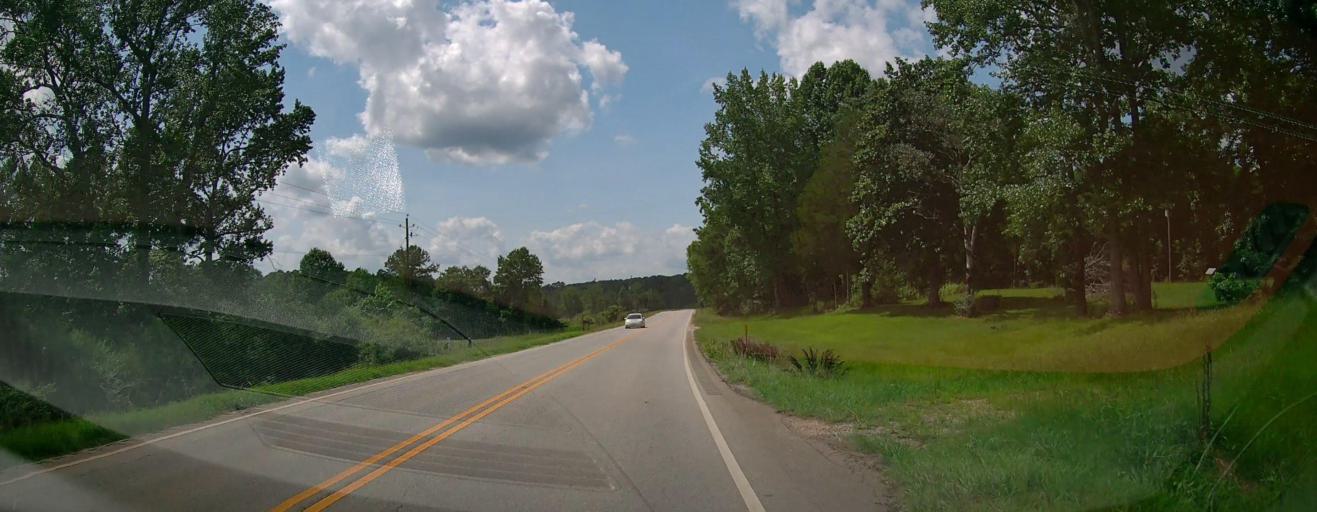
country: US
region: Alabama
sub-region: Cleburne County
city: Heflin
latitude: 33.5764
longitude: -85.4584
